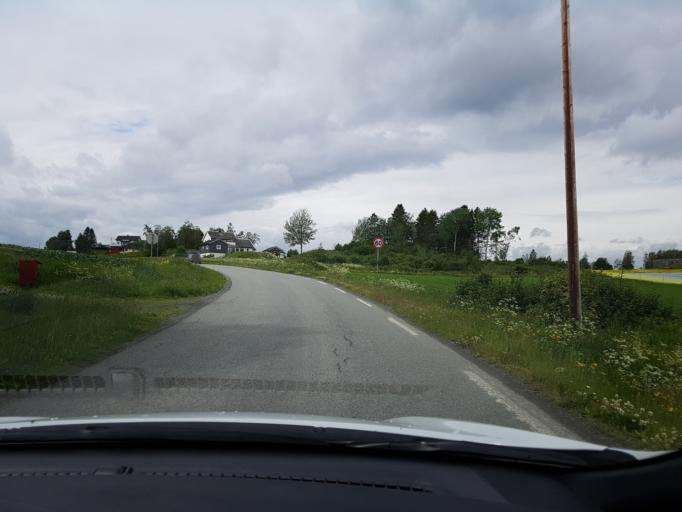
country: NO
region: Nord-Trondelag
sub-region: Frosta
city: Frosta
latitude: 63.6320
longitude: 10.7815
